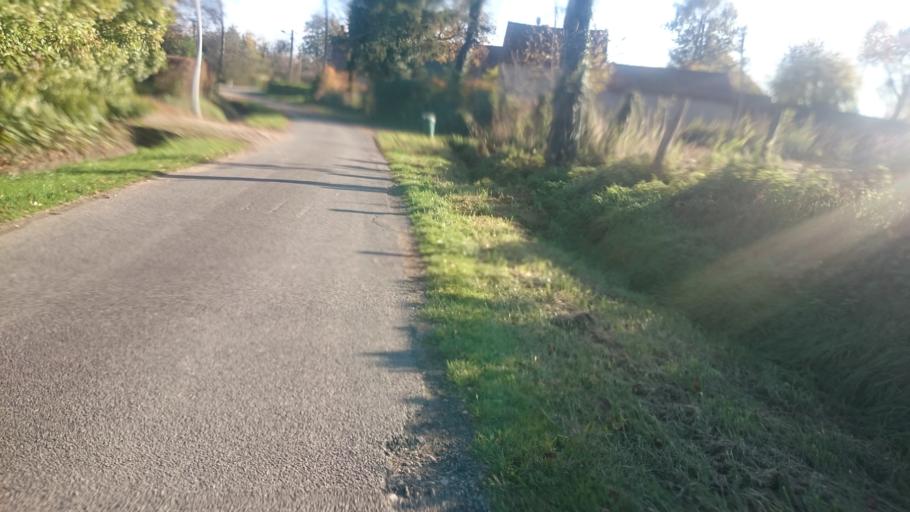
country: FR
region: Bourgogne
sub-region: Departement de Saone-et-Loire
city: Simandre
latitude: 46.6055
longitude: 4.9623
